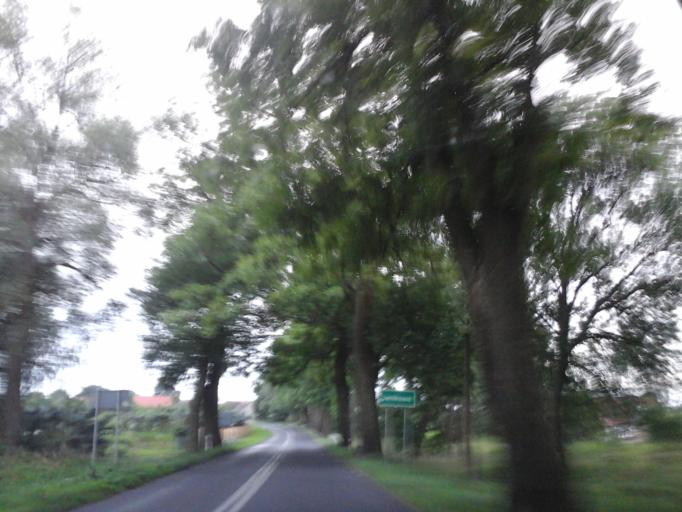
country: PL
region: West Pomeranian Voivodeship
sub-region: Powiat goleniowski
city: Nowogard
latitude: 53.5834
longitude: 15.1393
